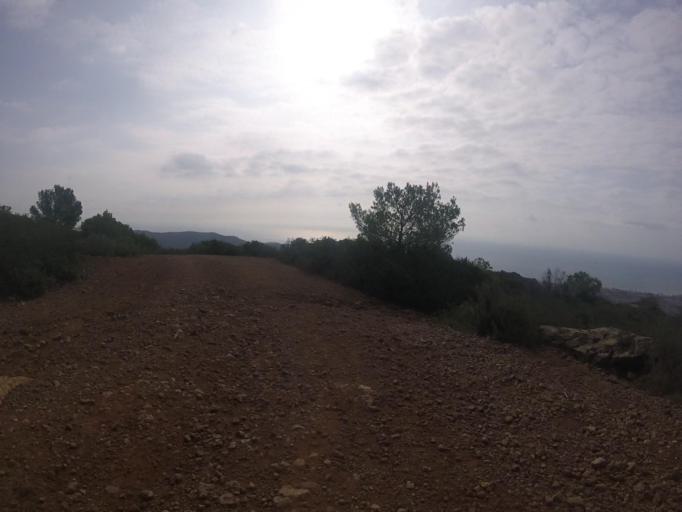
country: ES
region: Valencia
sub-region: Provincia de Castello
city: Benicassim
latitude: 40.0850
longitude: 0.0403
